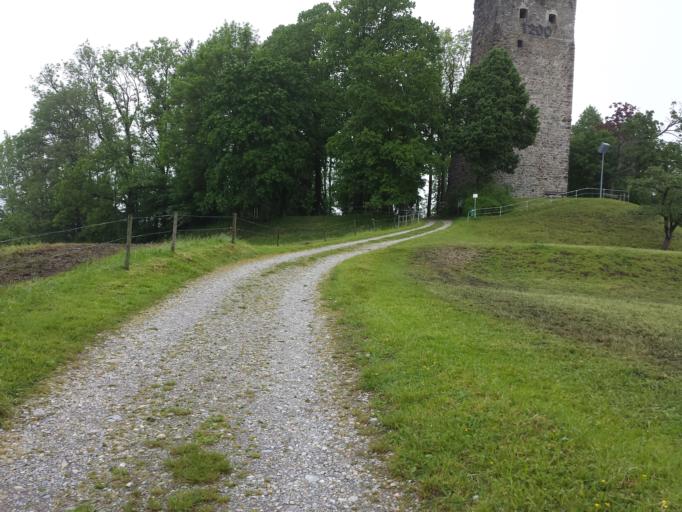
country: DE
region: Bavaria
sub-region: Swabia
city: Hergensweiler
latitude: 47.6370
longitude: 9.7557
